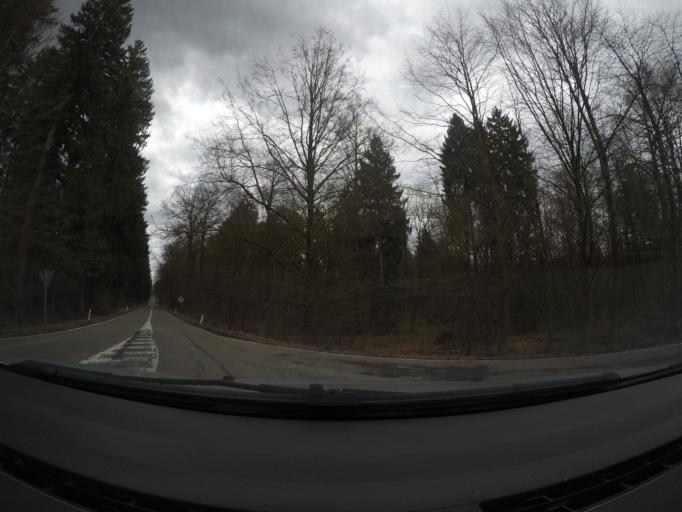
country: BE
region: Wallonia
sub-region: Province du Luxembourg
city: Leglise
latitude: 49.7627
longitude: 5.4784
